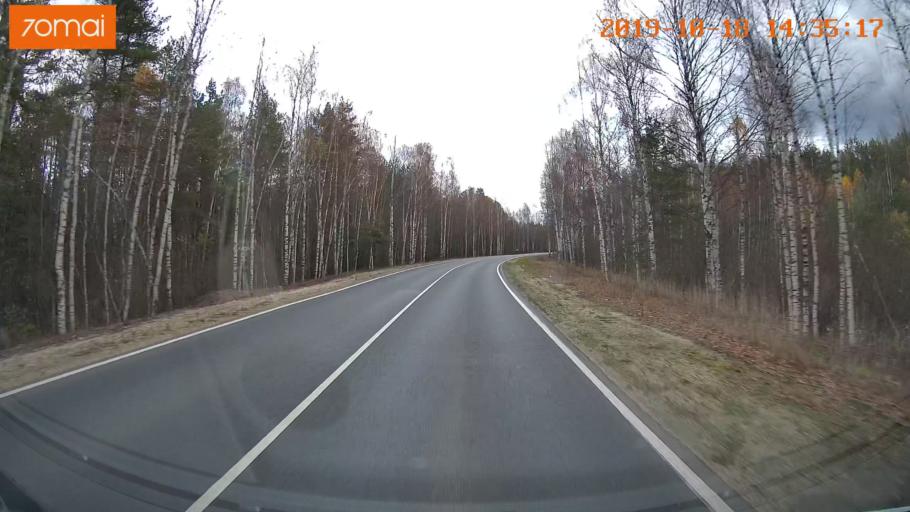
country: RU
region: Vladimir
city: Velikodvorskiy
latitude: 55.2216
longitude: 40.6334
